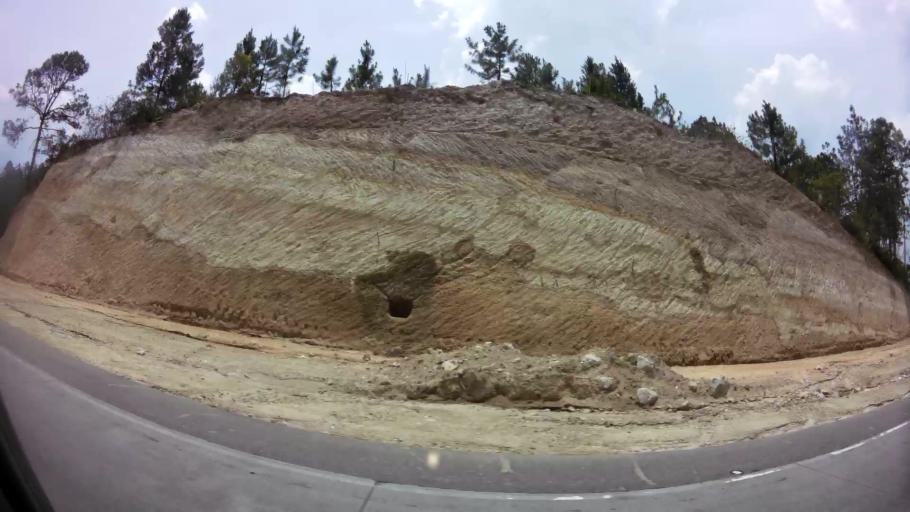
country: HN
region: Comayagua
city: El Socorro
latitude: 14.6373
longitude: -87.9248
